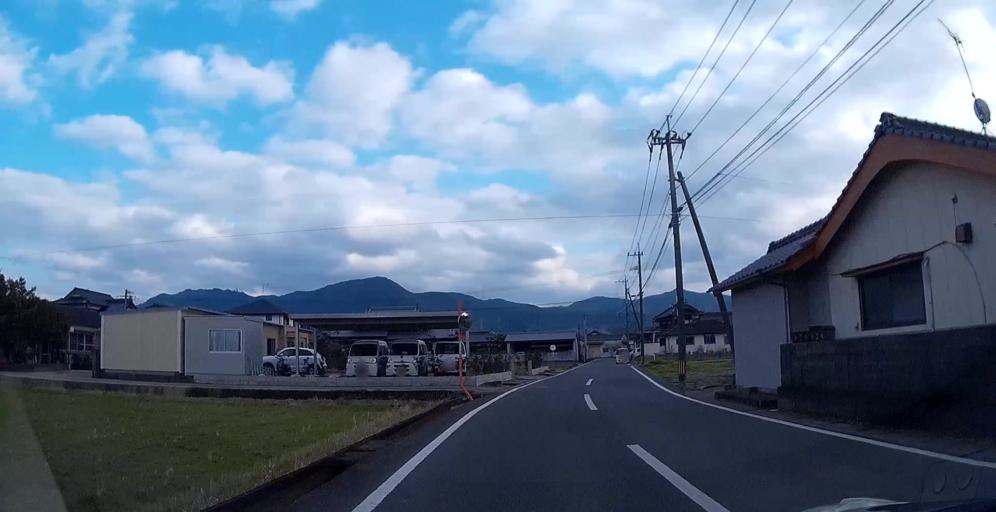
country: JP
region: Kumamoto
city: Yatsushiro
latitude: 32.5326
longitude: 130.6369
